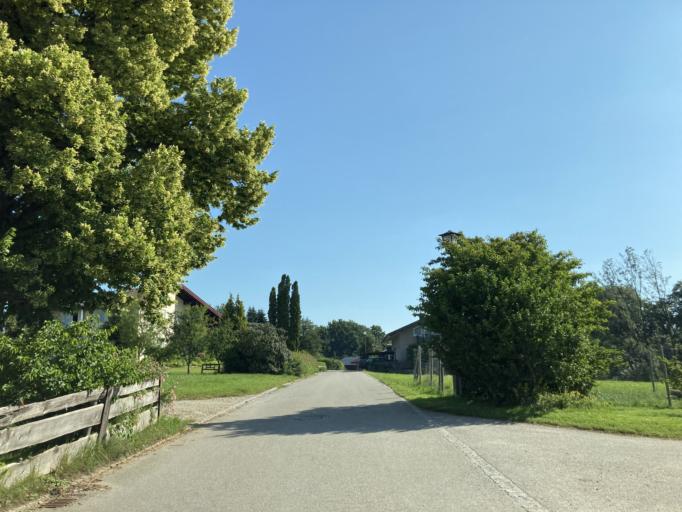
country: DE
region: Bavaria
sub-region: Upper Bavaria
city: Bad Endorf
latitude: 47.9003
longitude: 12.2798
